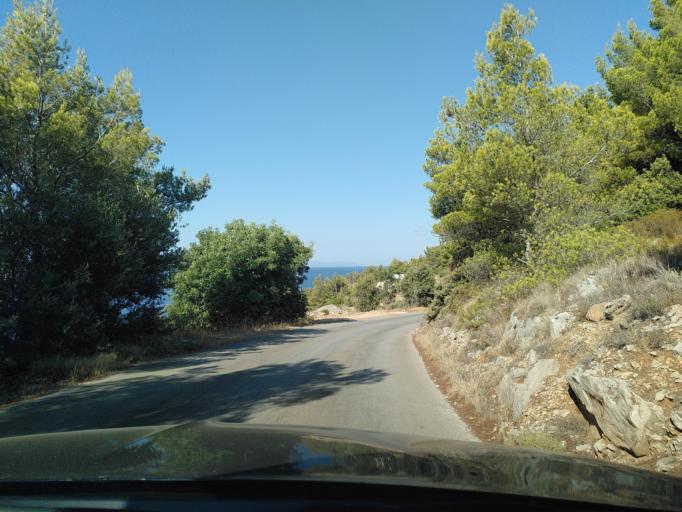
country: HR
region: Splitsko-Dalmatinska
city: Jelsa
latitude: 43.1234
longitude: 16.6714
